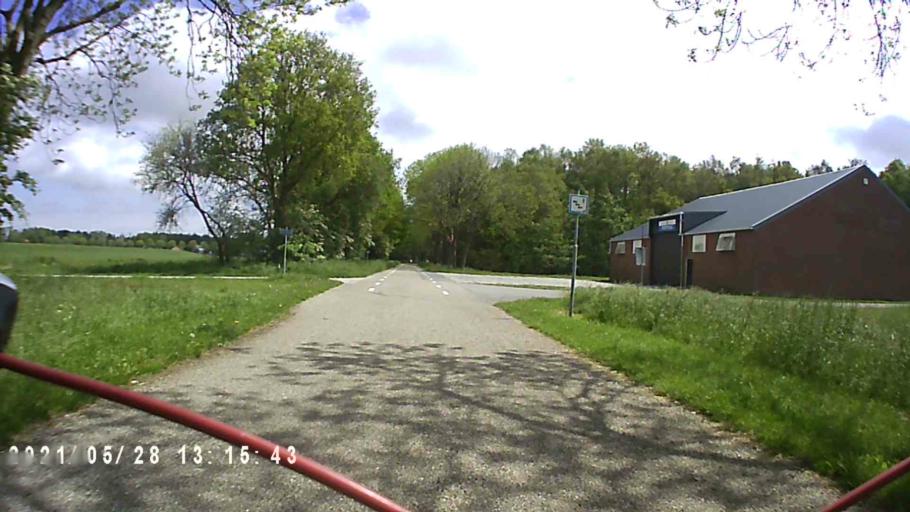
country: NL
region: Groningen
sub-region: Gemeente  Oldambt
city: Winschoten
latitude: 53.1772
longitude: 7.0367
